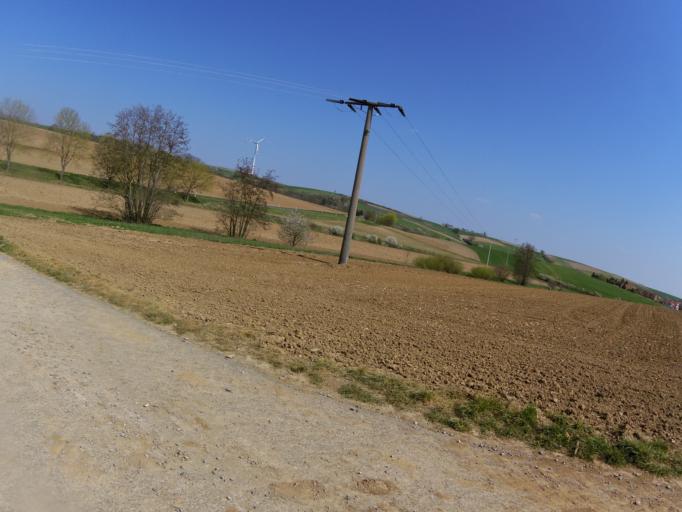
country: DE
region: Bavaria
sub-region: Regierungsbezirk Unterfranken
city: Dettelbach
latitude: 49.8204
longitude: 10.1418
